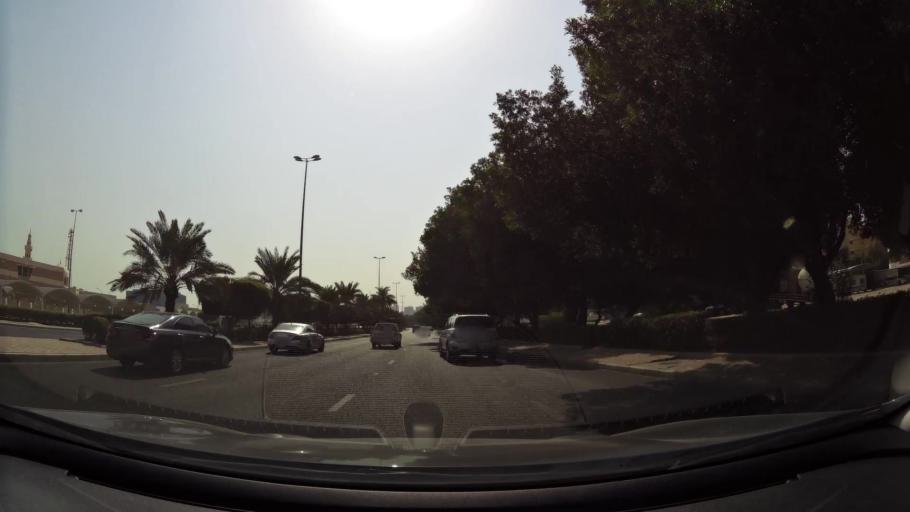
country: KW
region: Al Ahmadi
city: Al Fintas
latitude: 29.1690
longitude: 48.1229
